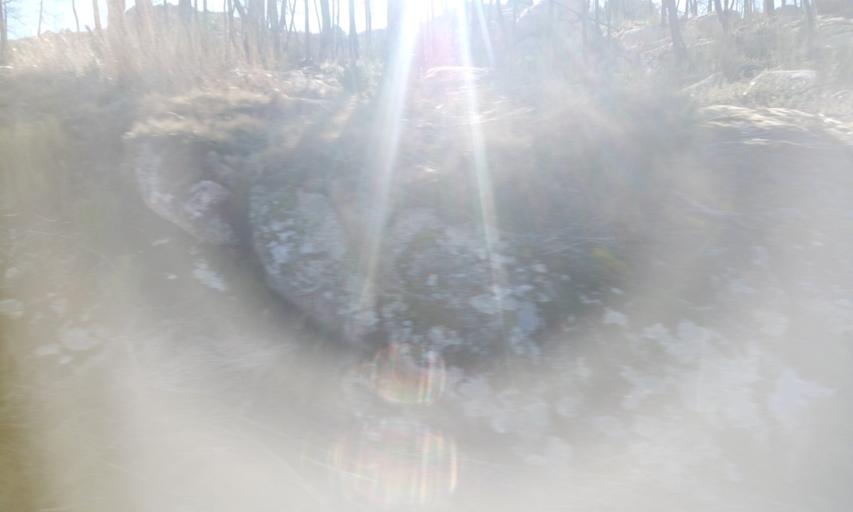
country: PT
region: Guarda
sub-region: Manteigas
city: Manteigas
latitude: 40.4863
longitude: -7.5199
